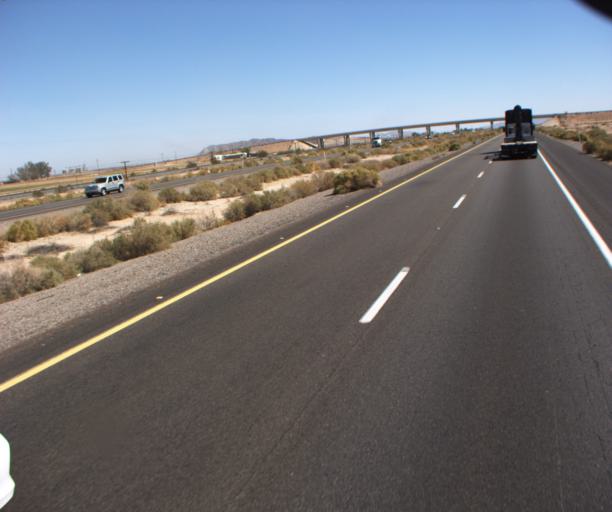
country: US
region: Arizona
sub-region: Yuma County
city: Wellton
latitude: 32.6738
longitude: -114.0783
